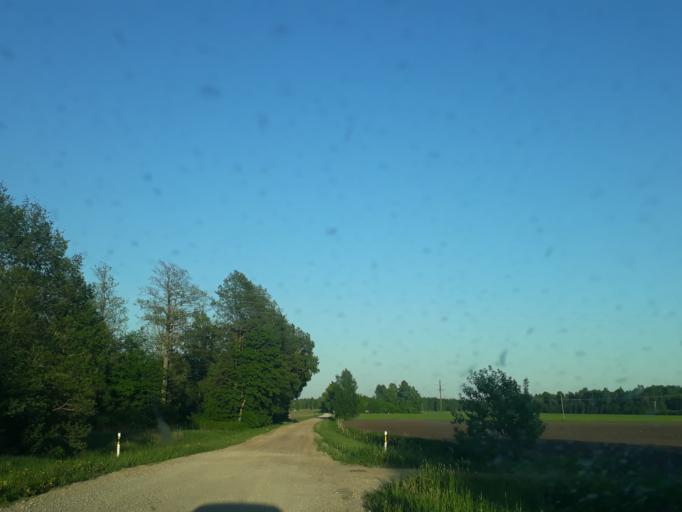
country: EE
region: Paernumaa
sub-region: Tootsi vald
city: Tootsi
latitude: 58.5856
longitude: 24.8975
